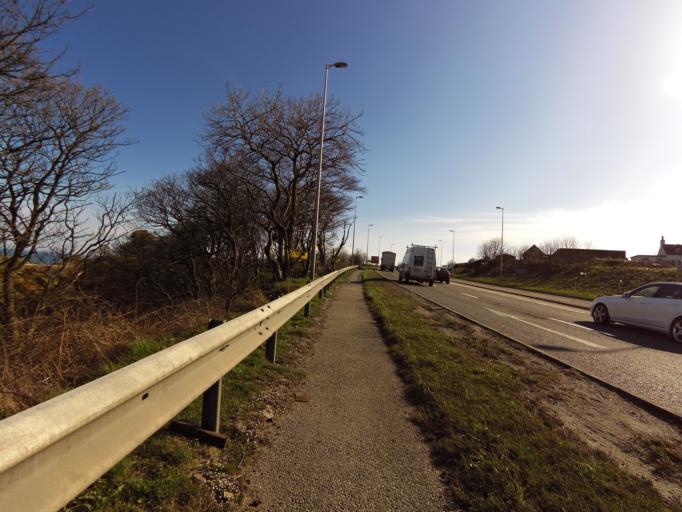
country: GB
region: Scotland
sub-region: Aberdeenshire
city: Newtonhill
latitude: 57.0067
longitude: -2.1737
